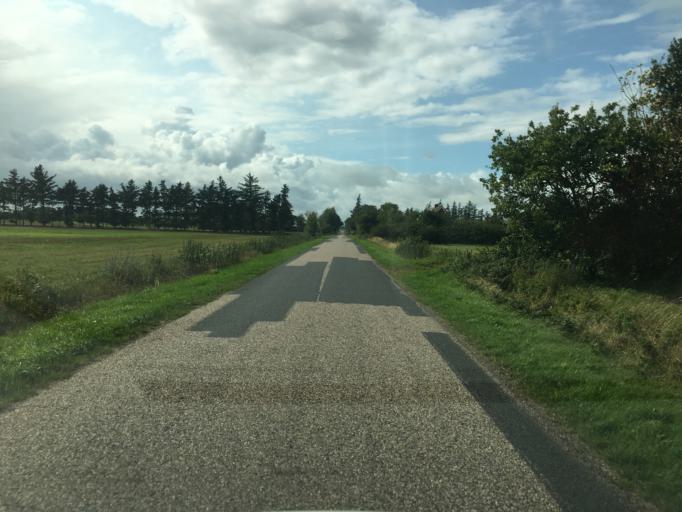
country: DK
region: South Denmark
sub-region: Tonder Kommune
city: Tonder
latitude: 54.9788
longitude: 8.8389
